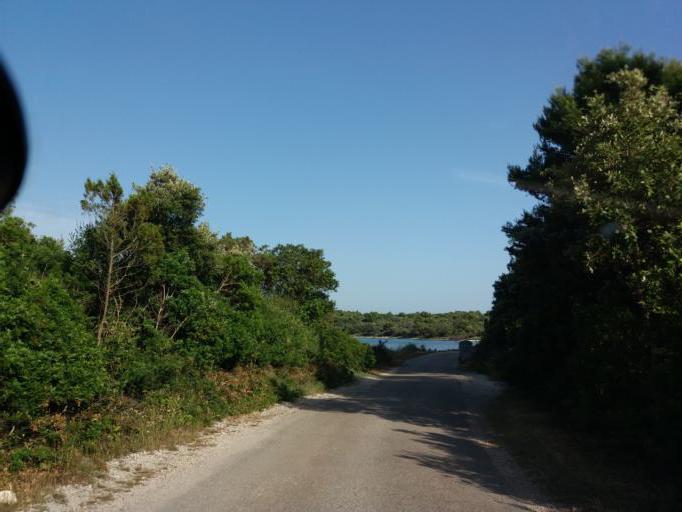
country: HR
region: Zadarska
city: Ugljan
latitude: 44.1477
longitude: 14.8326
